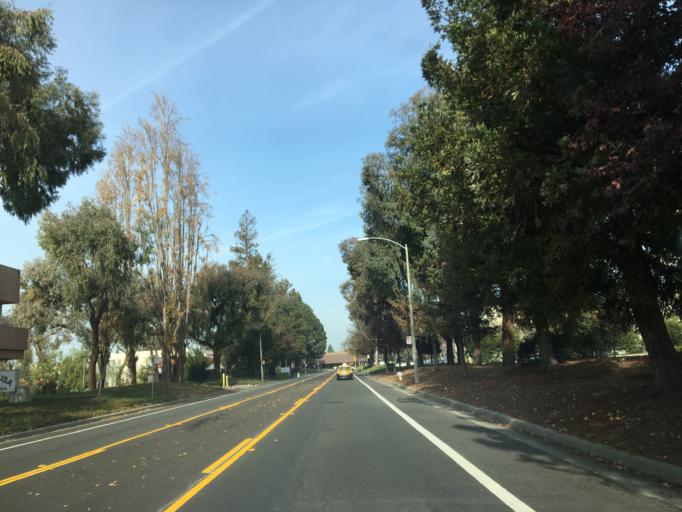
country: US
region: California
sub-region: Santa Clara County
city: Sunnyvale
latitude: 37.4095
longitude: -122.0044
